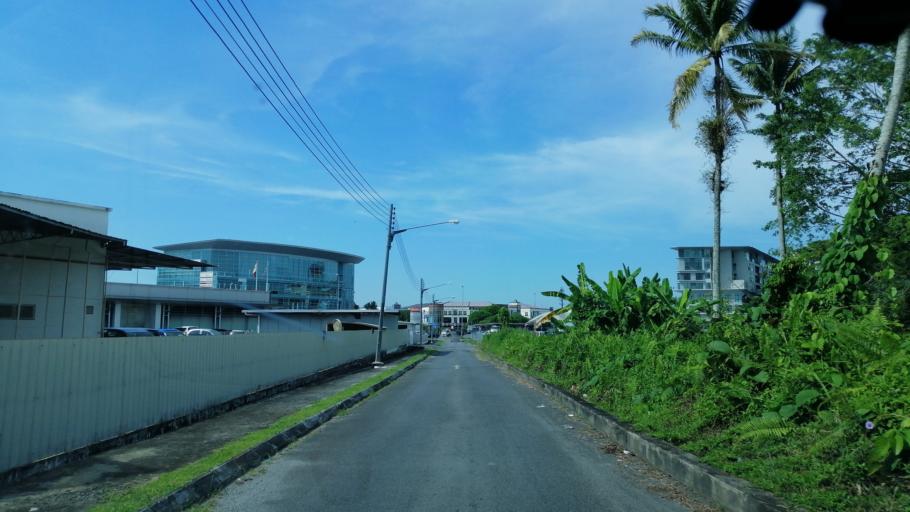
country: MY
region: Sarawak
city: Kuching
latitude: 1.5192
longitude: 110.3527
